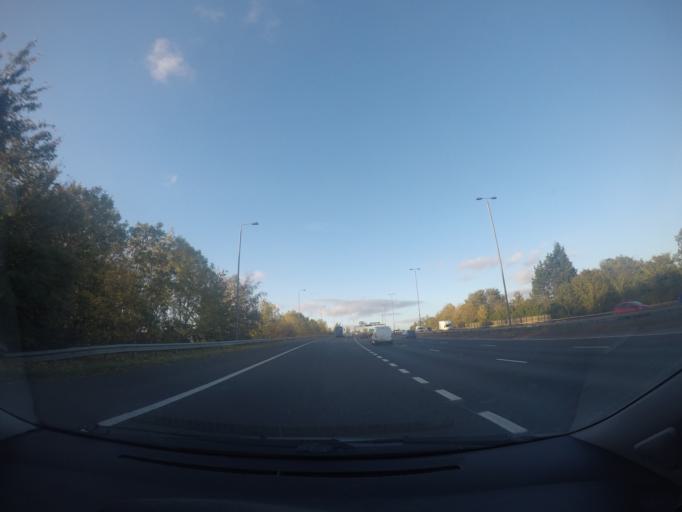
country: GB
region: England
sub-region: City and Borough of Leeds
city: Aberford
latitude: 53.8424
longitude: -1.3422
